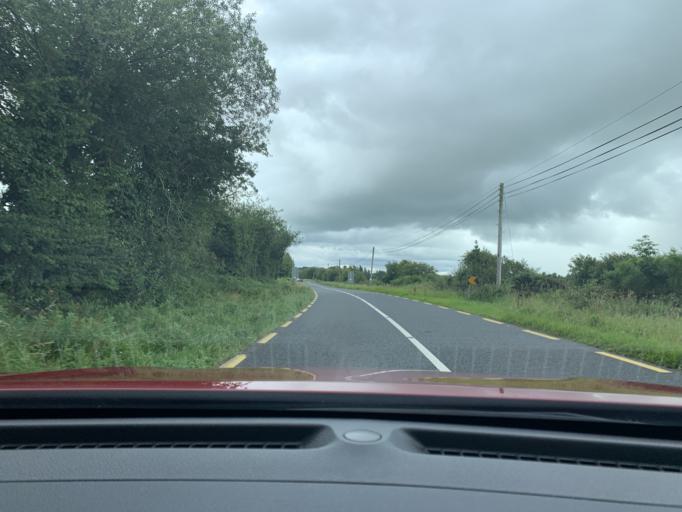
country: IE
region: Ulster
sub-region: County Donegal
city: Convoy
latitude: 54.8007
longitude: -7.6357
